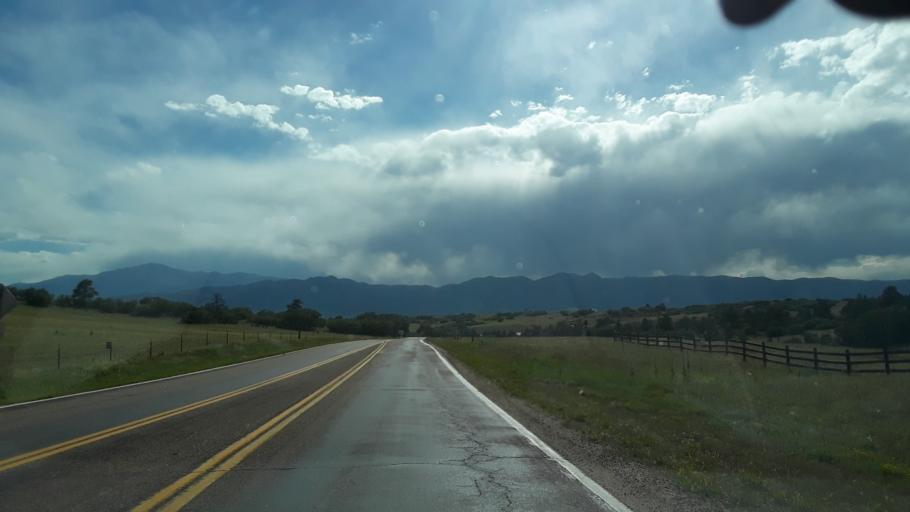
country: US
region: Colorado
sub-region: El Paso County
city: Gleneagle
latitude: 39.0124
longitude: -104.7704
